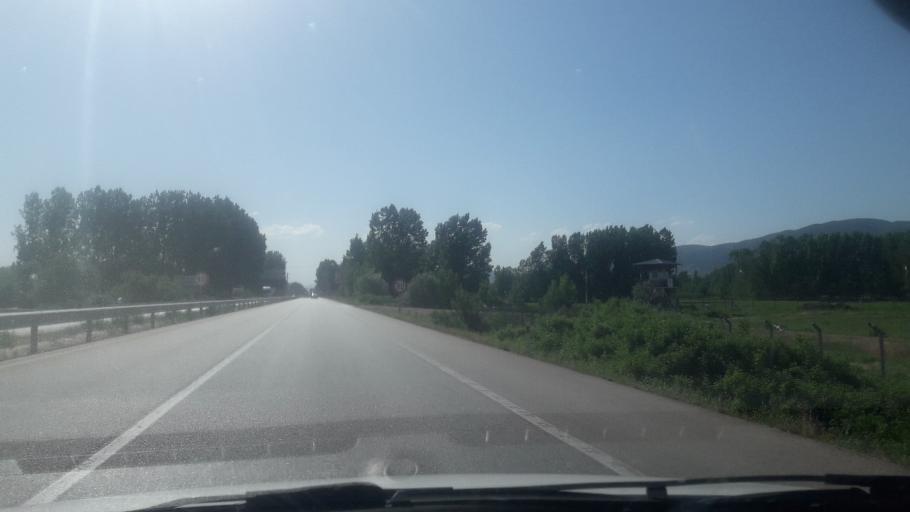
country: TR
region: Tokat
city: Yesilyurt
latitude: 40.2994
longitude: 36.3549
